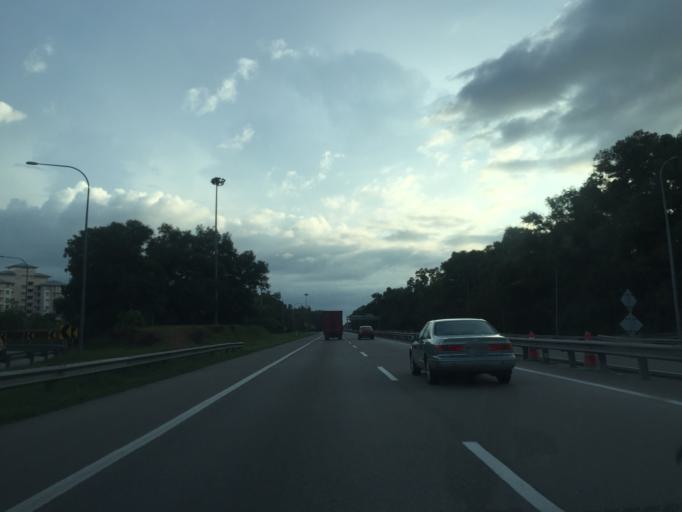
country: MY
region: Kedah
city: Sungai Petani
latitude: 5.6738
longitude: 100.5155
